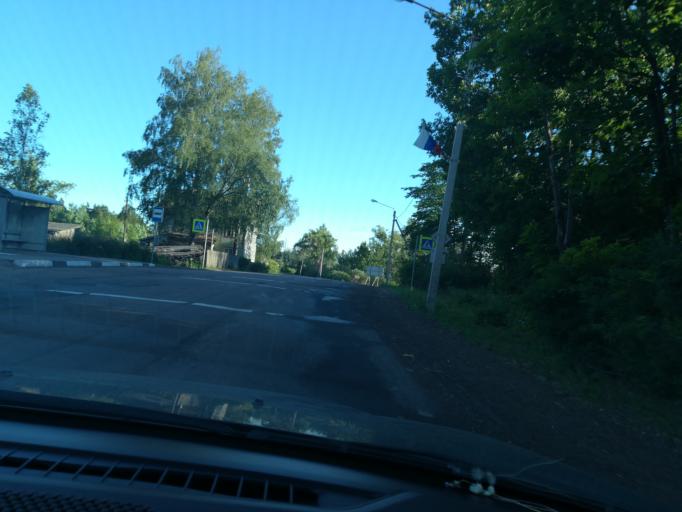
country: RU
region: Leningrad
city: Lesogorskiy
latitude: 61.0435
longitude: 28.9267
